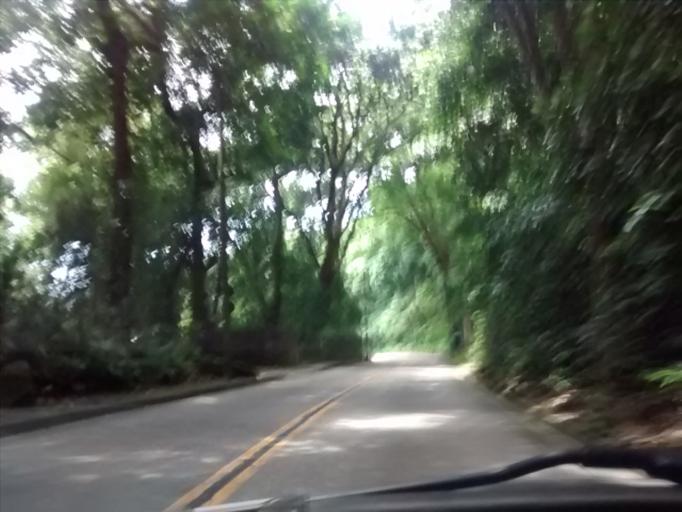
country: BR
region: Rio de Janeiro
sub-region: Rio De Janeiro
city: Rio de Janeiro
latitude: -22.9894
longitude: -43.2741
